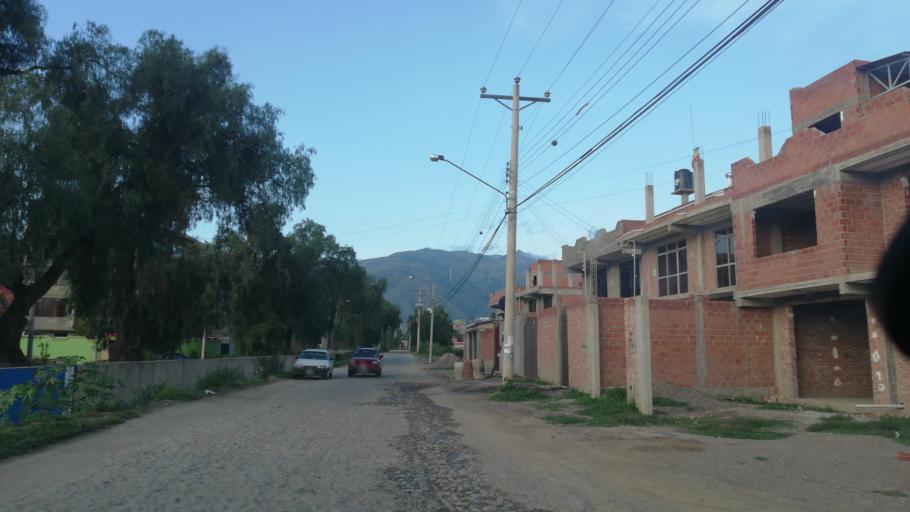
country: BO
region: Cochabamba
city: Cochabamba
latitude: -17.3817
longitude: -66.2081
